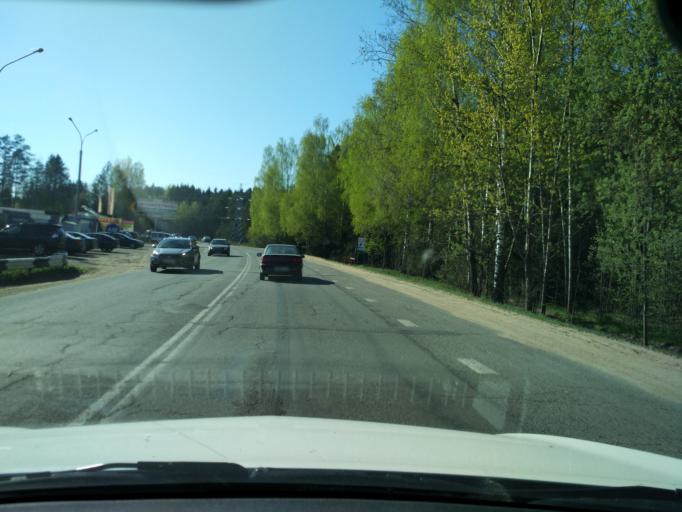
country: BY
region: Minsk
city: Lyeskawka
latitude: 53.9595
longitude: 27.7211
